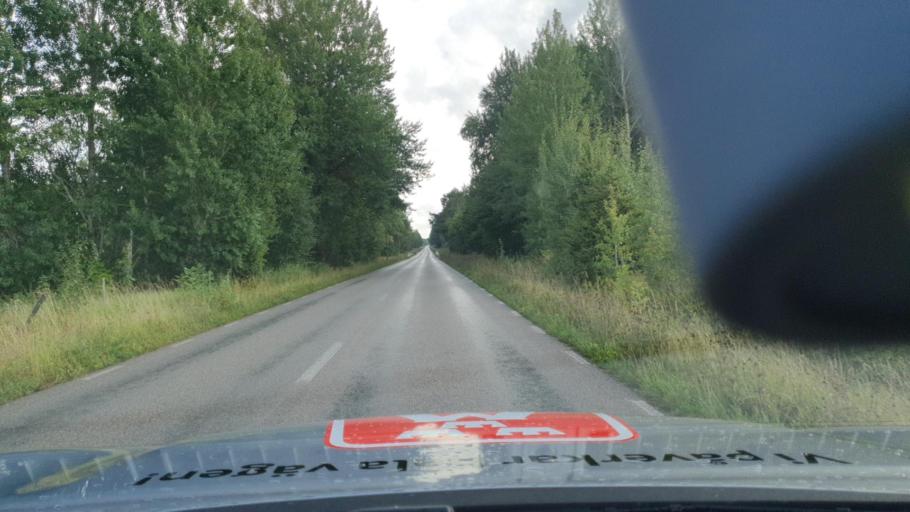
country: SE
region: Gotland
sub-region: Gotland
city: Slite
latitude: 57.6438
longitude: 18.7676
